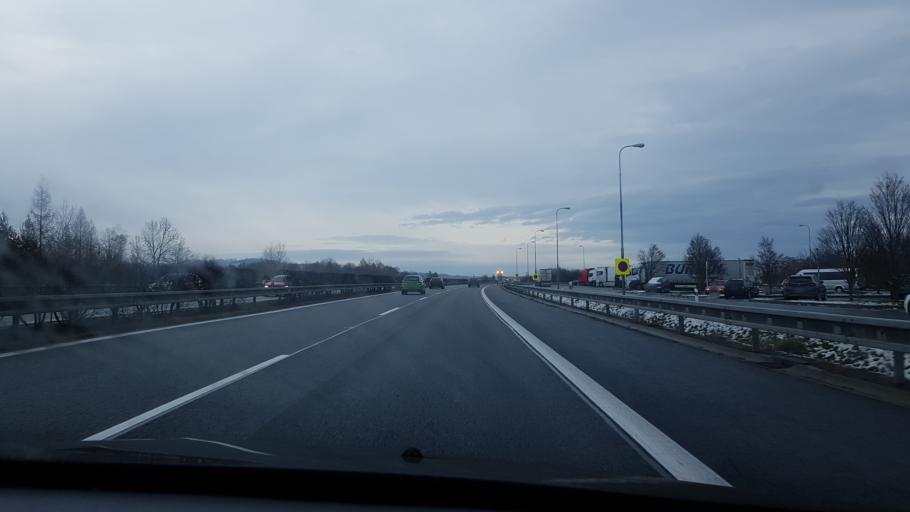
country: CZ
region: Olomoucky
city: Velky Ujezd
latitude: 49.5807
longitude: 17.4613
